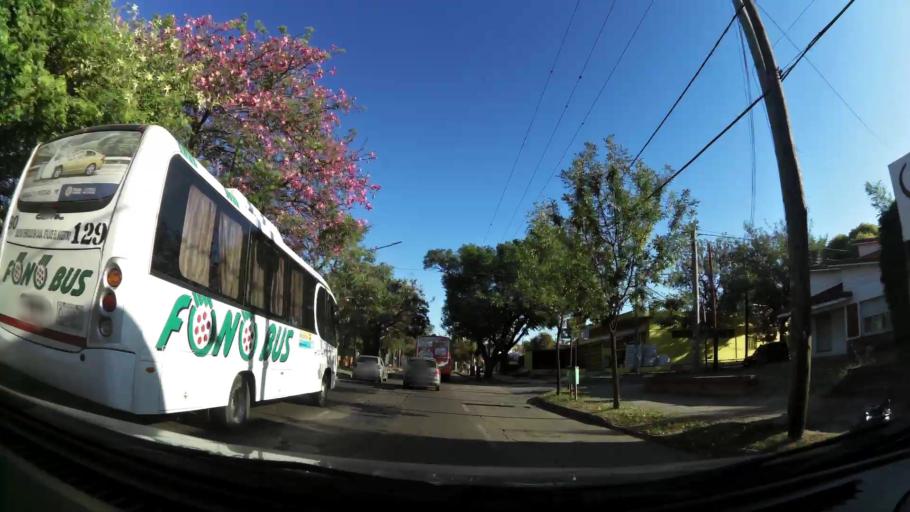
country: AR
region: Cordoba
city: Villa Allende
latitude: -31.3458
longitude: -64.2508
